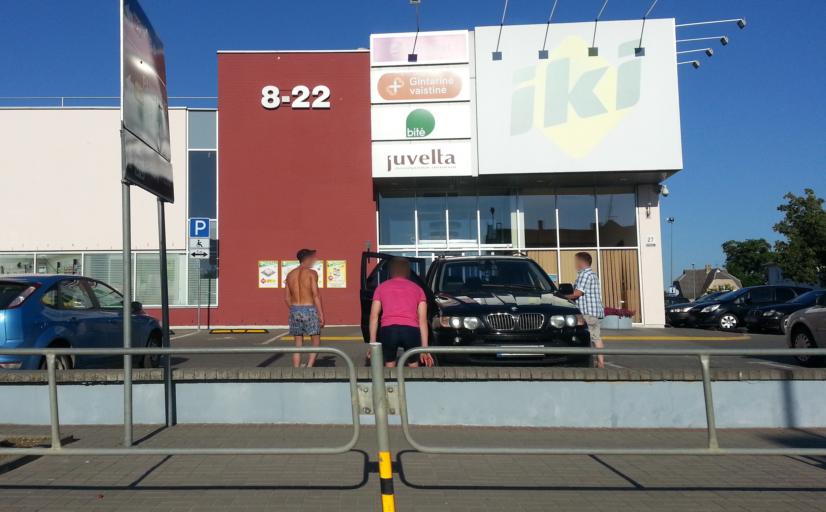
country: LT
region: Panevezys
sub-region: Birzai
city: Birzai
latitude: 56.2012
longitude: 24.7564
